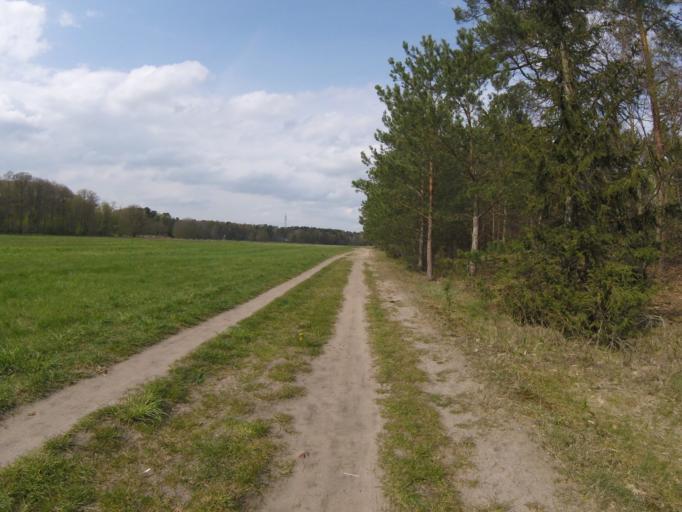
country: DE
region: Brandenburg
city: Bestensee
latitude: 52.2303
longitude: 13.6045
